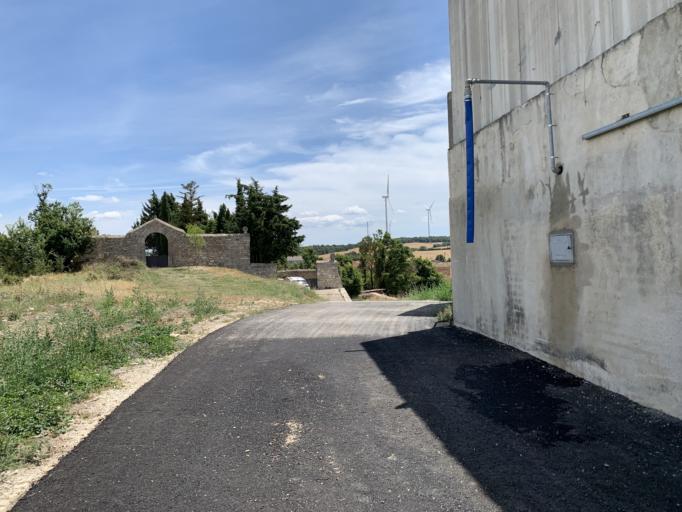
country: ES
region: Catalonia
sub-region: Provincia de Tarragona
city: Vallfogona de Riucorb
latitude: 41.5447
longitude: 1.2654
